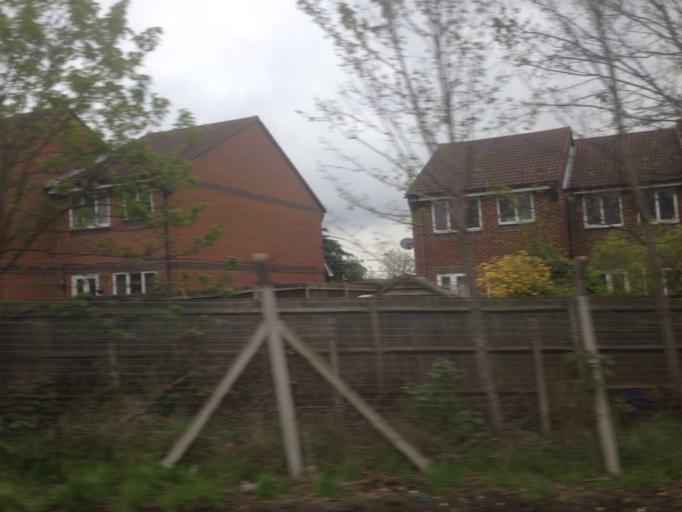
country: GB
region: England
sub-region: Greater London
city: Mitcham
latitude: 51.4139
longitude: -0.1480
